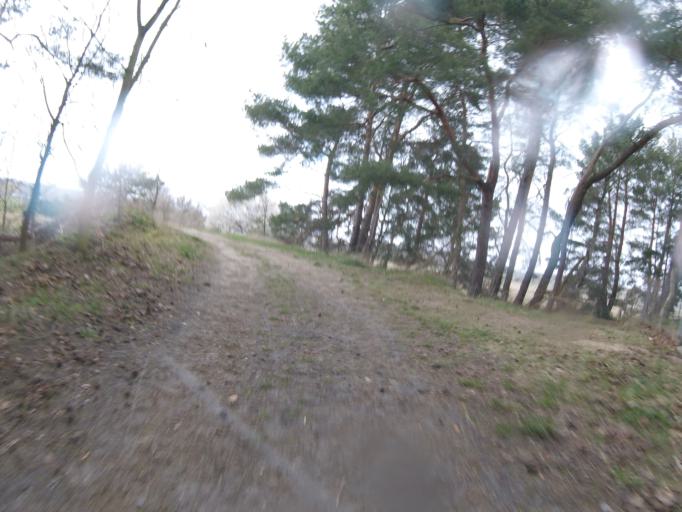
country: DE
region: Brandenburg
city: Schwerin
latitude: 52.2012
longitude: 13.5909
